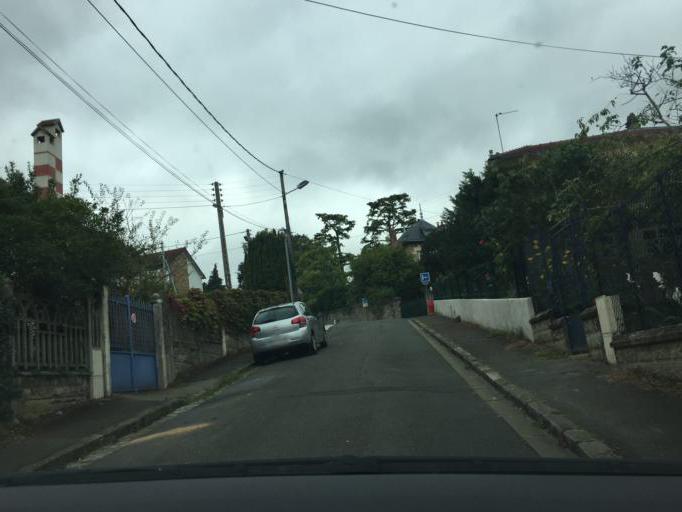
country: FR
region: Ile-de-France
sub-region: Departement de l'Essonne
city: Orsay
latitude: 48.7017
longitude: 2.1862
